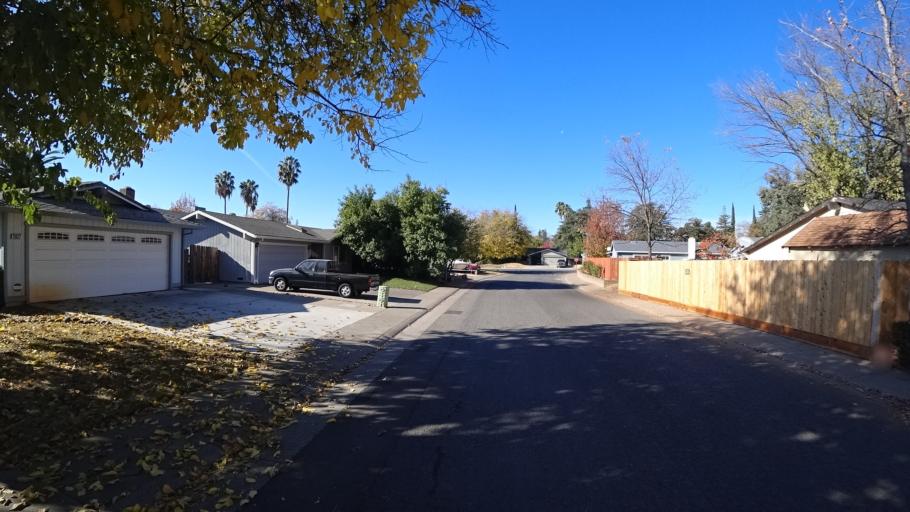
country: US
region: California
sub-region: Sacramento County
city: Antelope
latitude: 38.7123
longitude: -121.3104
